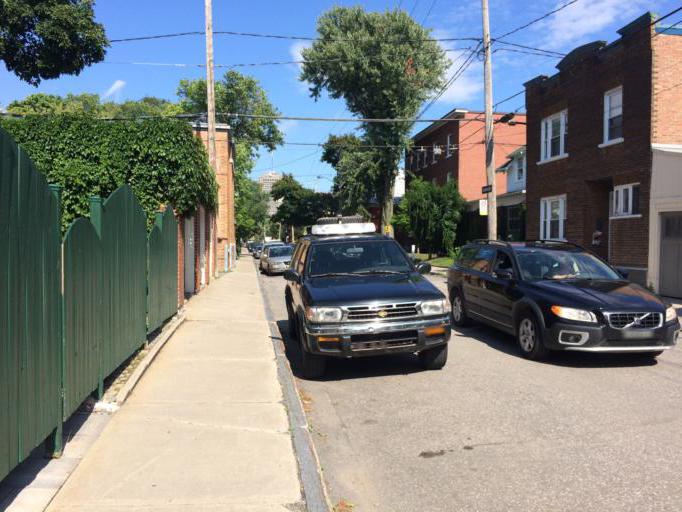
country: CA
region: Quebec
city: Quebec
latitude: 46.8021
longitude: -71.2288
